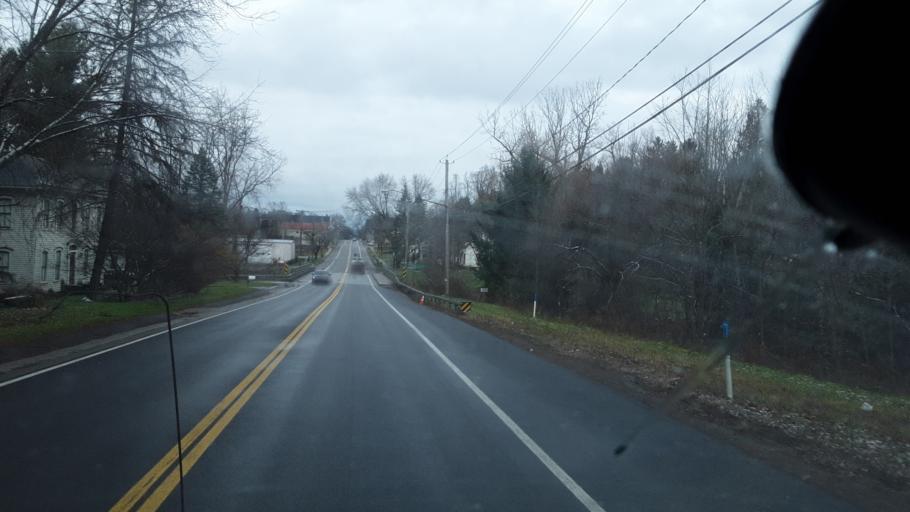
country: US
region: New York
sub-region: Cattaraugus County
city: Delevan
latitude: 42.4858
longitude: -78.4804
